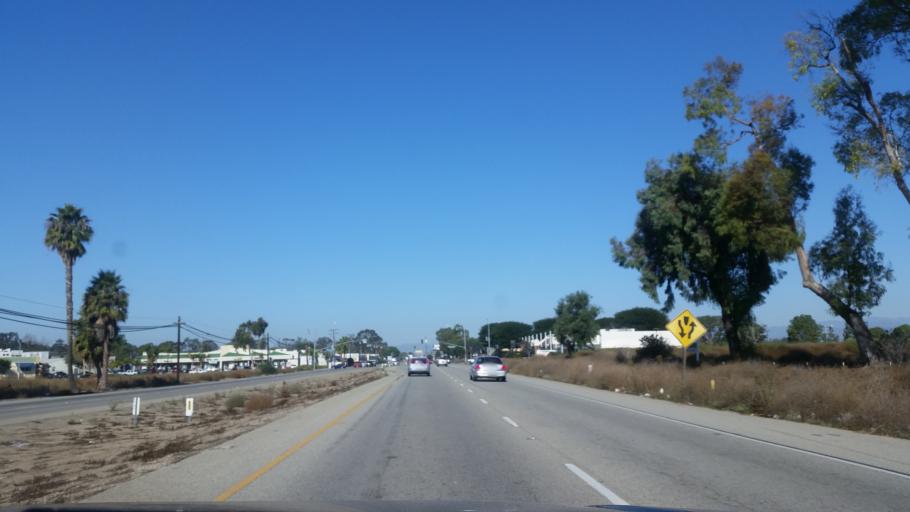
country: US
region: California
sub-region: Ventura County
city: Oxnard
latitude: 34.1785
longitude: -119.1633
